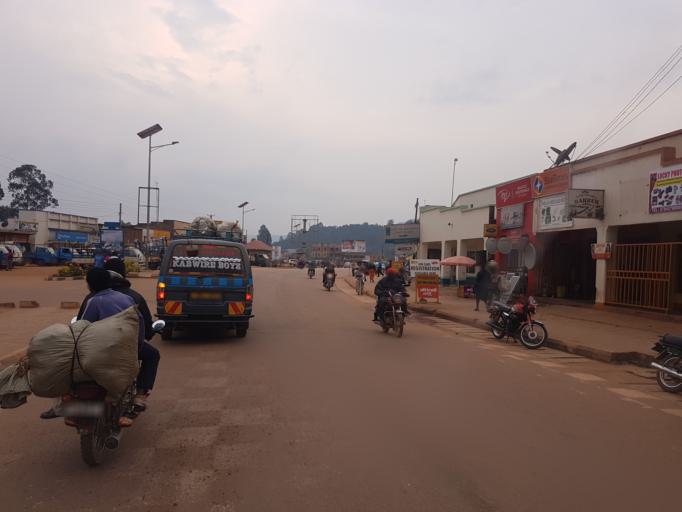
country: UG
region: Western Region
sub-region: Kabale District
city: Kabale
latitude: -1.2506
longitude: 29.9859
